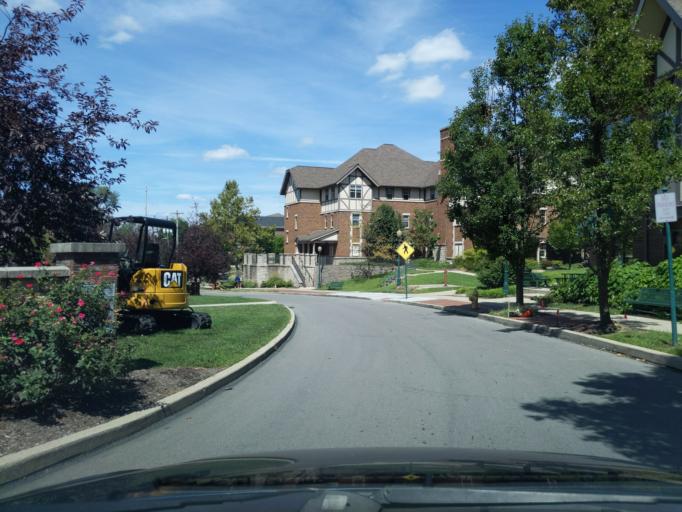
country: US
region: Ohio
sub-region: Hamilton County
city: Saint Bernard
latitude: 39.1310
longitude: -84.5221
